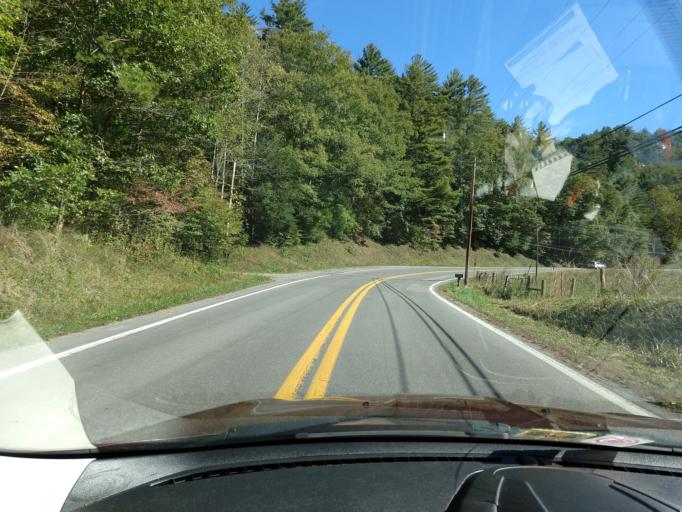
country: US
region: West Virginia
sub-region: Pocahontas County
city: Marlinton
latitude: 38.2127
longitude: -80.0390
